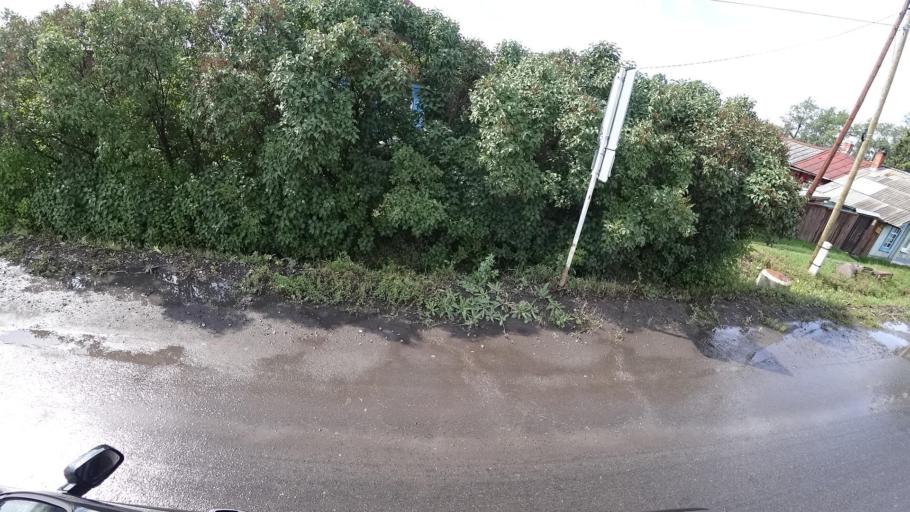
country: RU
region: Sverdlovsk
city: Kamyshlov
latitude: 56.8390
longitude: 62.7323
